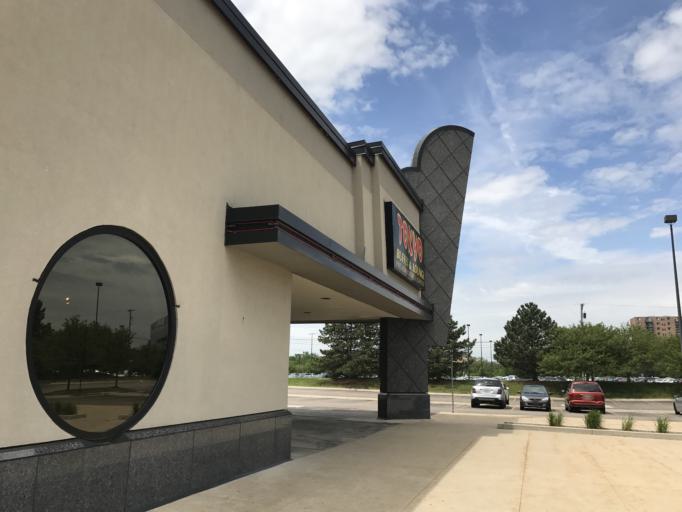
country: US
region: Michigan
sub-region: Oakland County
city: Franklin
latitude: 42.4993
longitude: -83.2950
